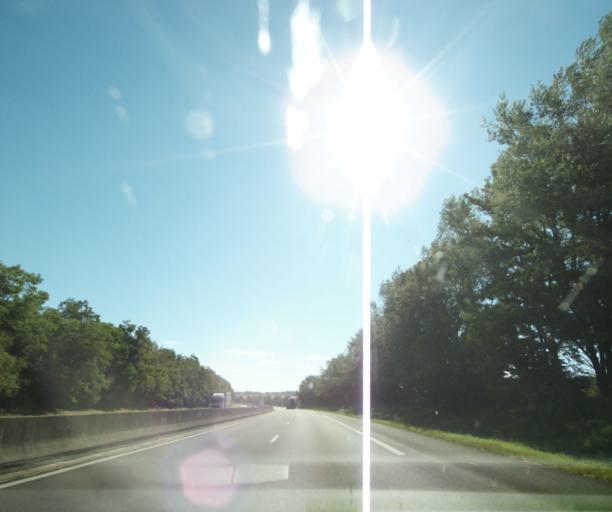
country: FR
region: Champagne-Ardenne
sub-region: Departement de la Haute-Marne
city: Avrecourt
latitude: 47.9523
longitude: 5.4302
